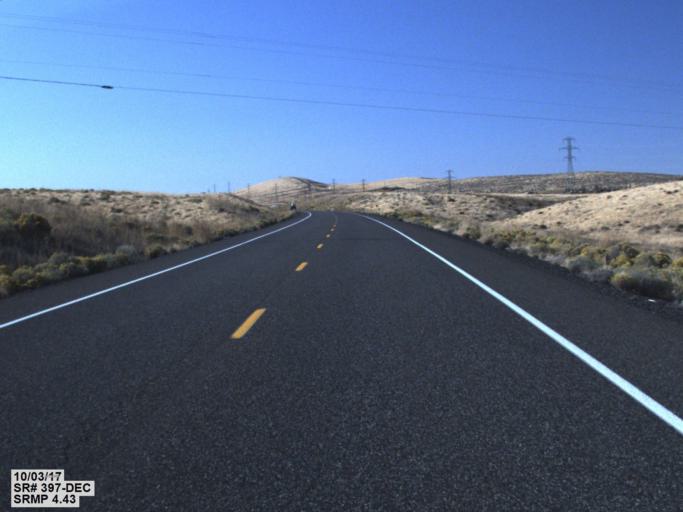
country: US
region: Washington
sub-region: Benton County
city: Highland
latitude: 46.1466
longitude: -119.1173
